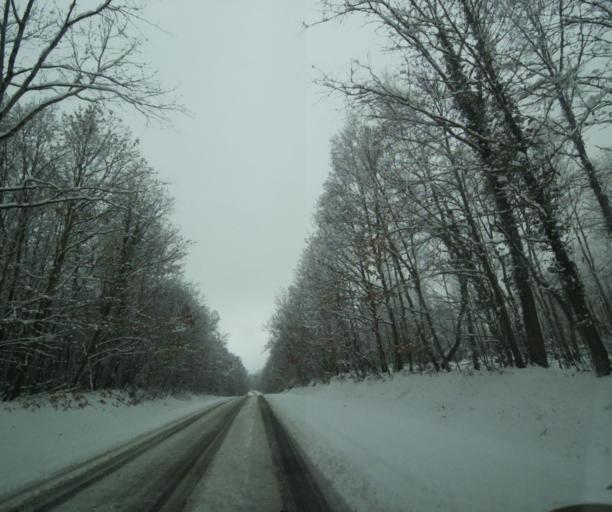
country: FR
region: Champagne-Ardenne
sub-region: Departement de la Haute-Marne
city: Montier-en-Der
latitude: 48.5298
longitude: 4.7893
